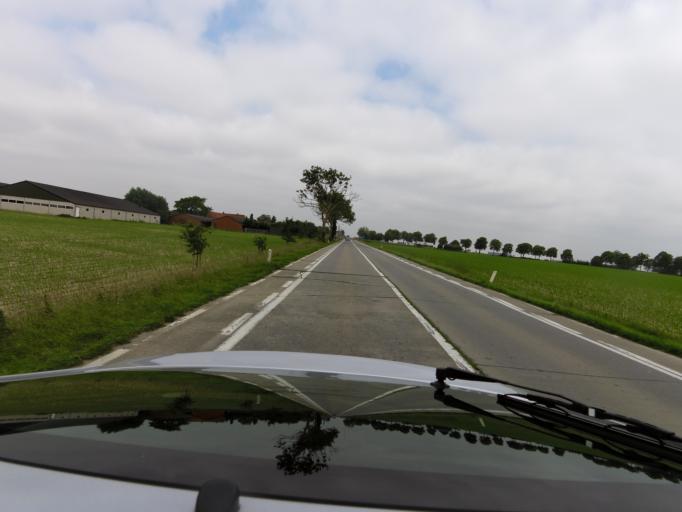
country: BE
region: Flanders
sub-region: Provincie West-Vlaanderen
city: Alveringem
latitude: 50.9696
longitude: 2.7019
